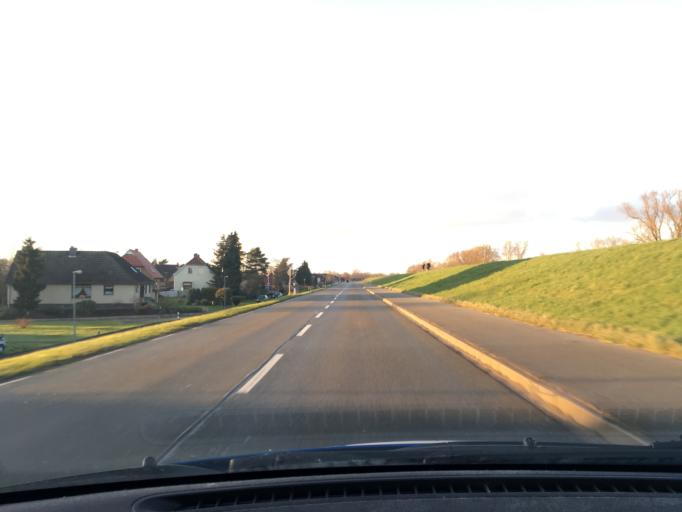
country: DE
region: Hamburg
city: Harburg
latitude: 53.4578
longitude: 10.0588
